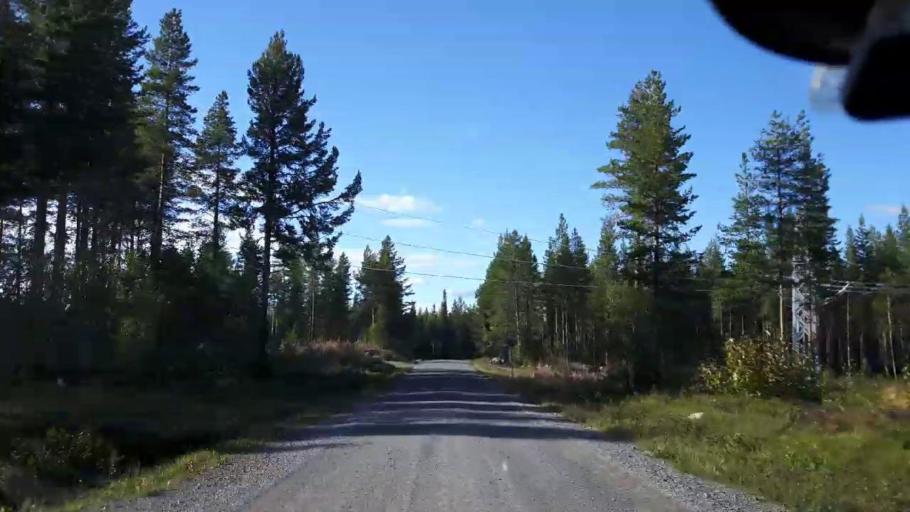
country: SE
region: Jaemtland
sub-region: Ragunda Kommun
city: Hammarstrand
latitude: 63.5345
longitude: 16.0717
